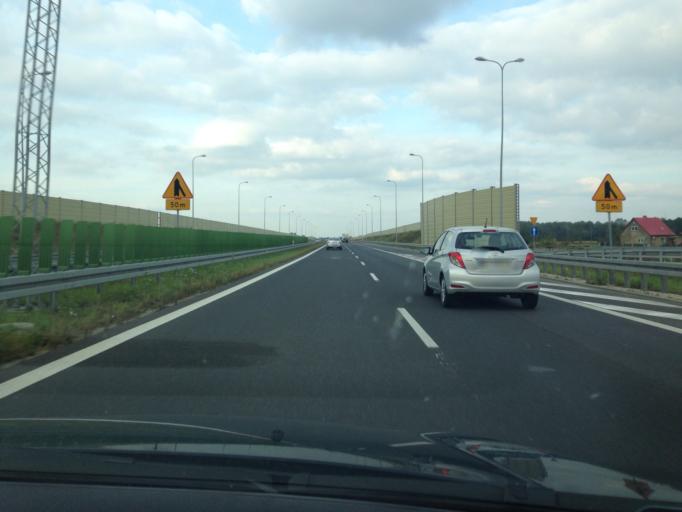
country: PL
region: Greater Poland Voivodeship
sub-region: Powiat gnieznienski
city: Lubowo
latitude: 52.4562
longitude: 17.3867
